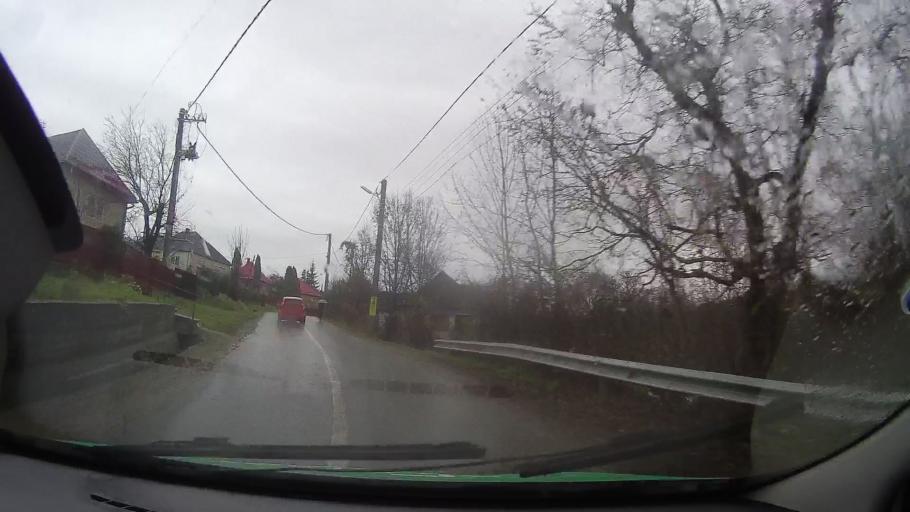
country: RO
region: Mures
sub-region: Comuna Vatava
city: Vatava
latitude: 46.9390
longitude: 24.7674
